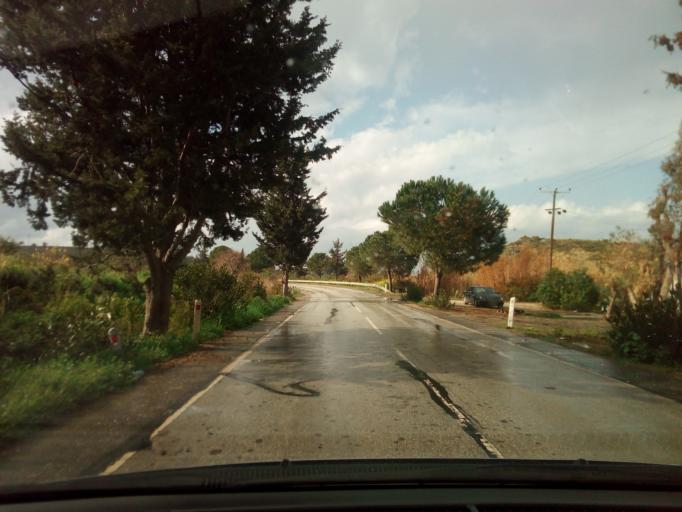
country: CY
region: Pafos
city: Polis
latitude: 35.0273
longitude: 32.4408
